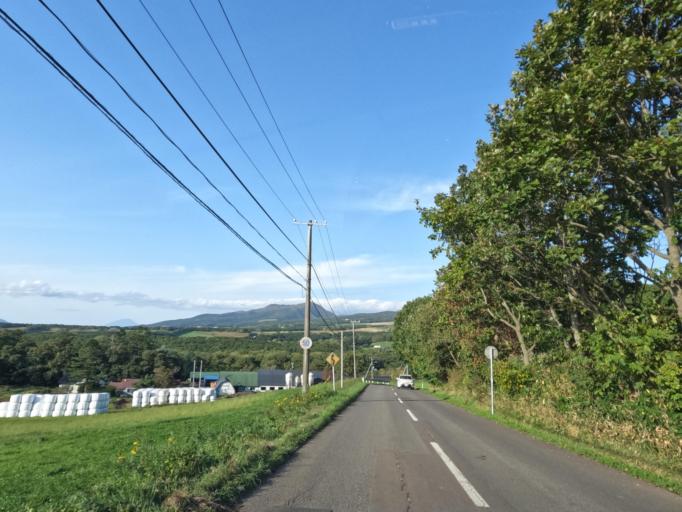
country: JP
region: Hokkaido
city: Muroran
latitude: 42.3949
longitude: 140.9340
